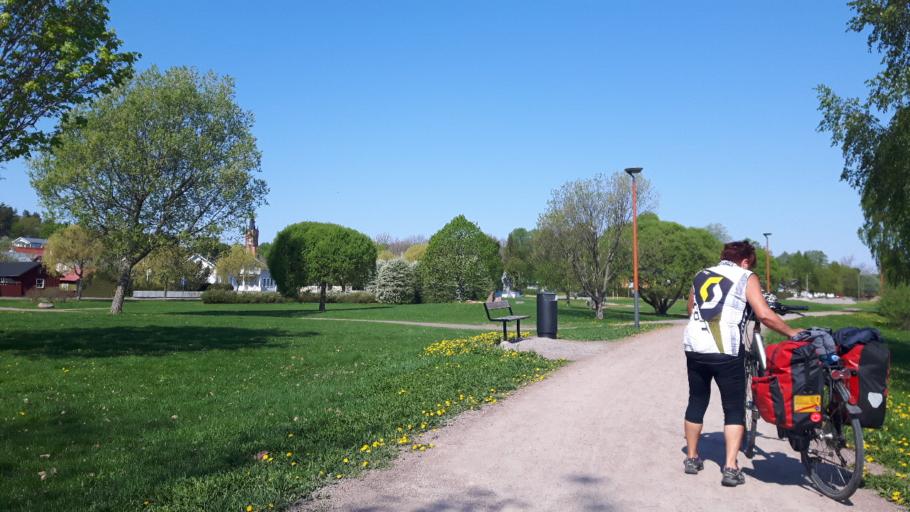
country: FI
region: Uusimaa
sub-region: Loviisa
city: Lovisa
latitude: 60.4533
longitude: 26.2342
